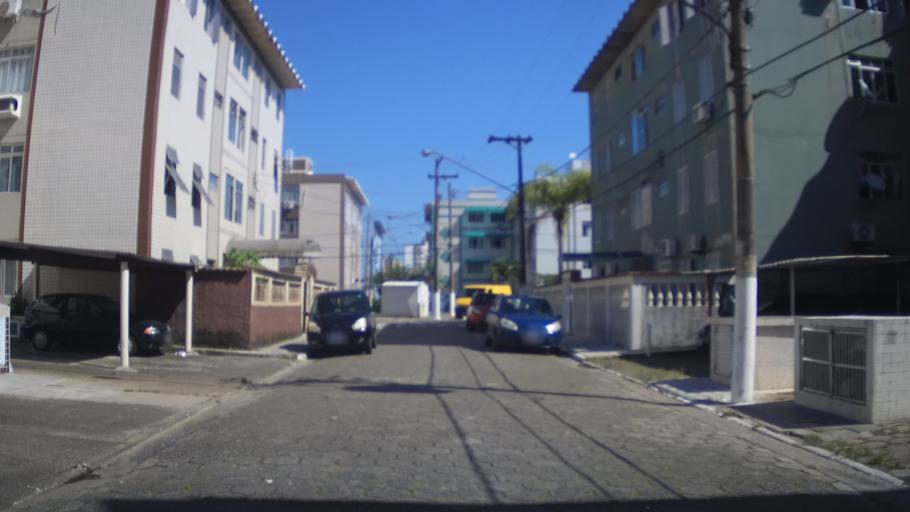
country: BR
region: Sao Paulo
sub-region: Praia Grande
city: Praia Grande
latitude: -24.0057
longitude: -46.4004
